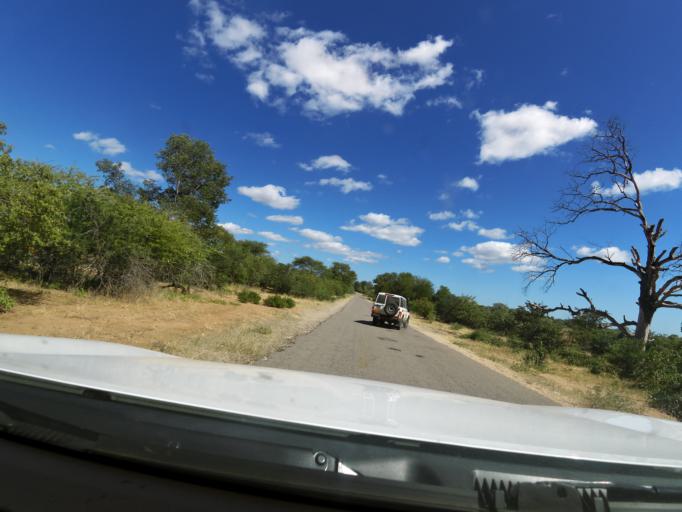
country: ZW
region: Matabeleland North
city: Kamativi Mine
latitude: -18.0074
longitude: 27.1465
